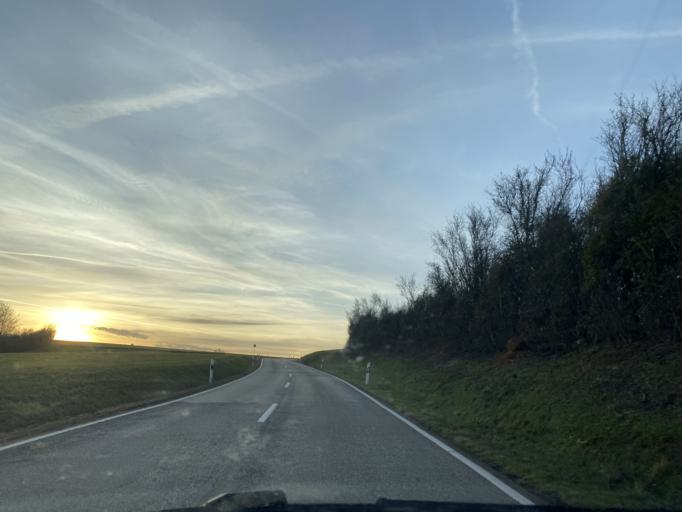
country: DE
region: Baden-Wuerttemberg
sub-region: Regierungsbezirk Stuttgart
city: Eberdingen
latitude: 48.8960
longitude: 8.9606
